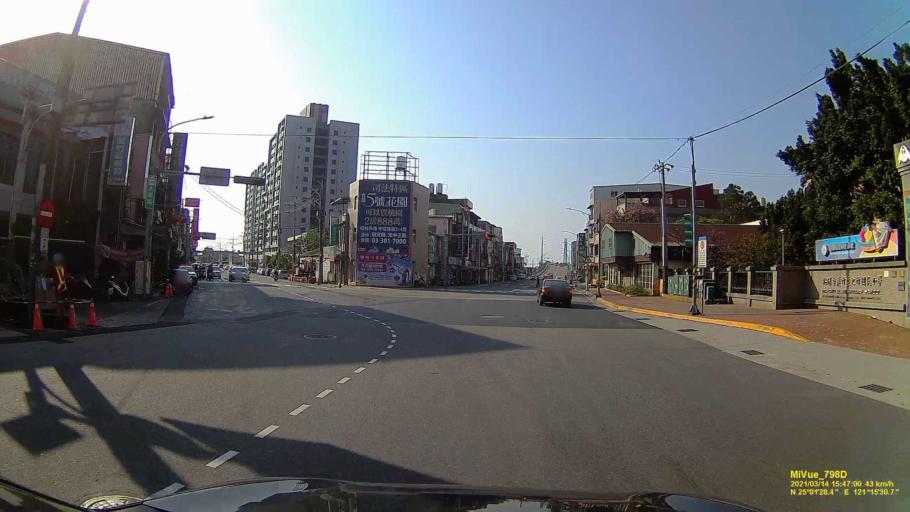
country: TW
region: Taiwan
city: Taoyuan City
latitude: 25.0247
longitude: 121.2583
